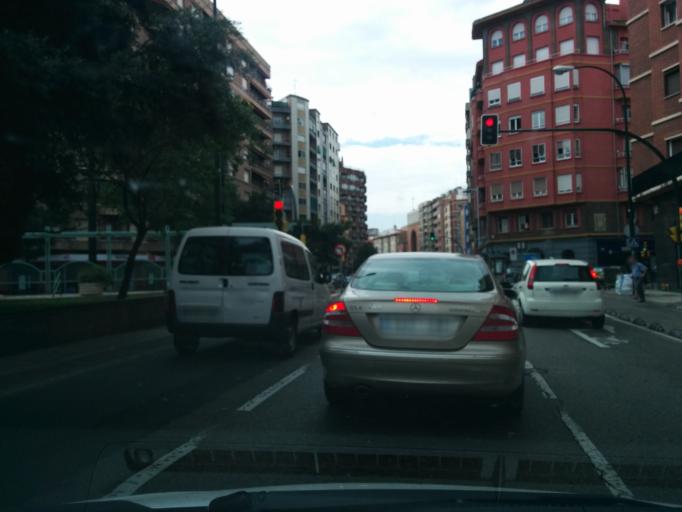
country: ES
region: Aragon
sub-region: Provincia de Zaragoza
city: Delicias
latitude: 41.6480
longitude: -0.8940
